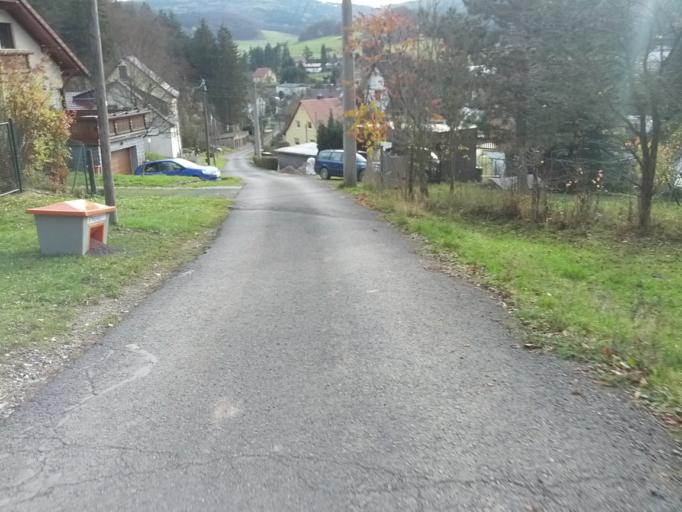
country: DE
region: Thuringia
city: Thal
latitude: 50.9393
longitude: 10.3508
